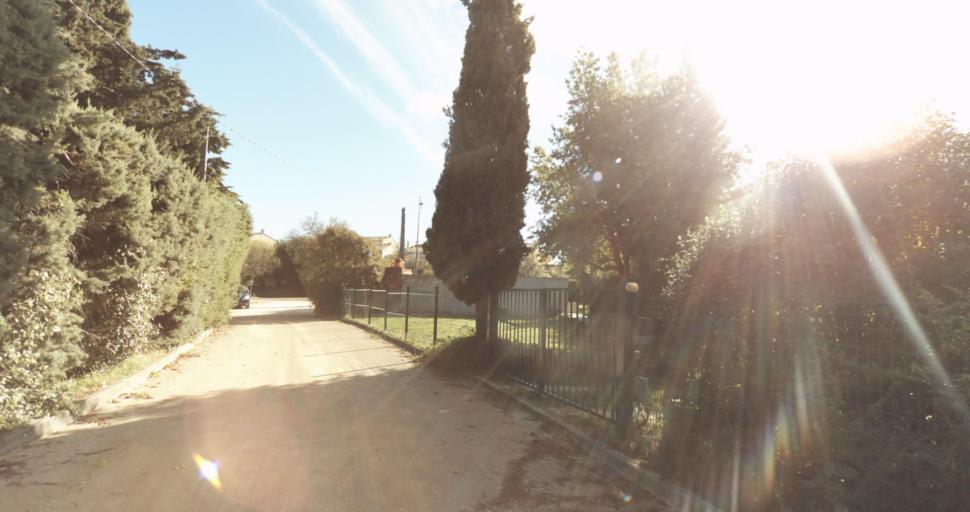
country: FR
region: Provence-Alpes-Cote d'Azur
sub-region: Departement des Bouches-du-Rhone
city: Venelles
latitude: 43.6017
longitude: 5.4882
